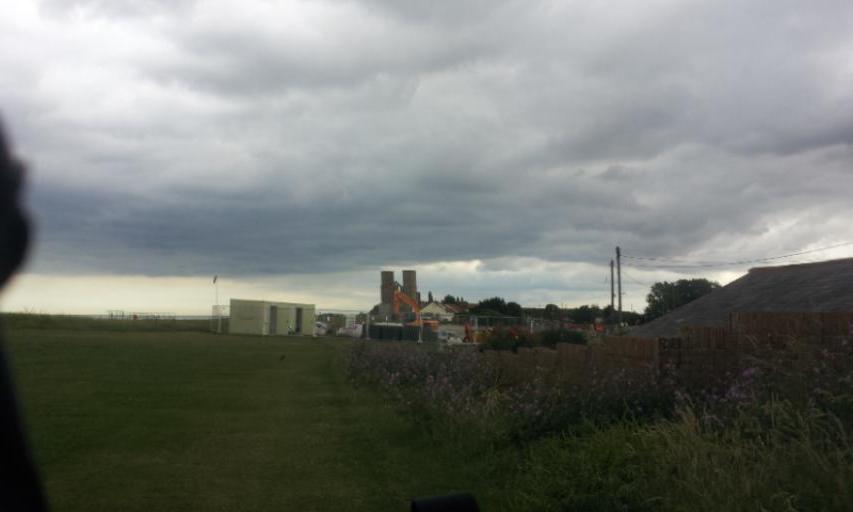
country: GB
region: England
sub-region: Kent
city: Herne Bay
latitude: 51.3780
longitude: 1.1940
